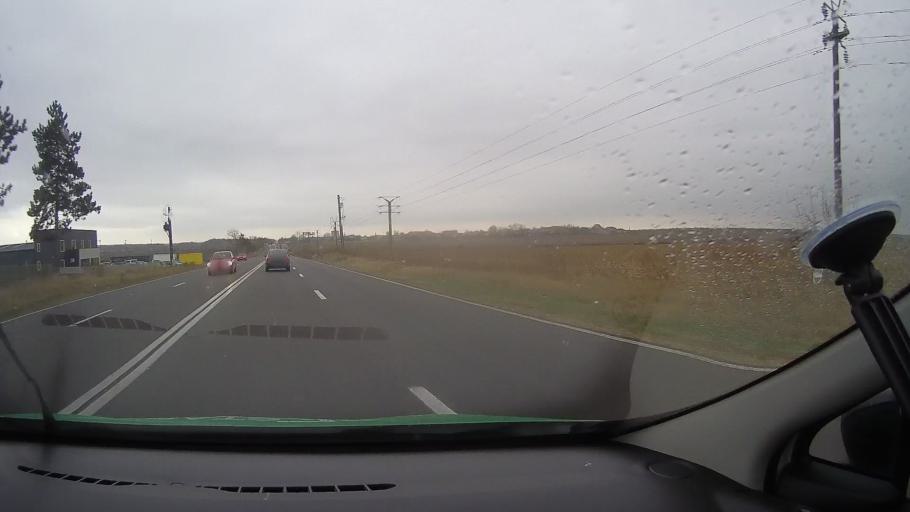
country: RO
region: Constanta
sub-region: Comuna Cumpana
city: Cumpana
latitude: 44.1658
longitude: 28.5290
